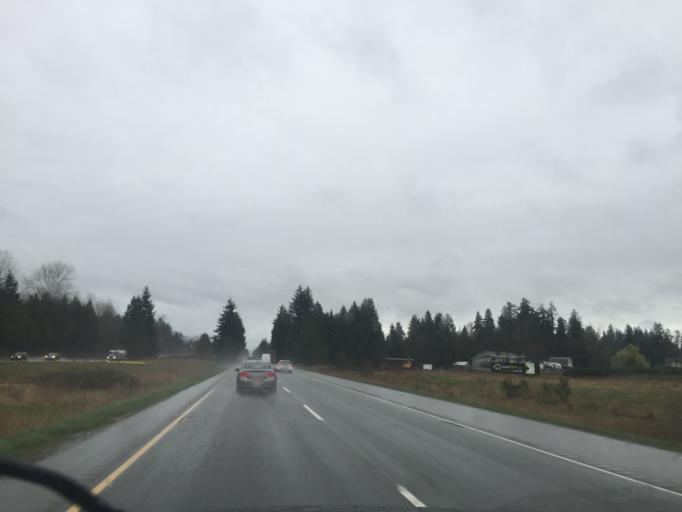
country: CA
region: British Columbia
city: Aldergrove
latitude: 49.0822
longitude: -122.4442
